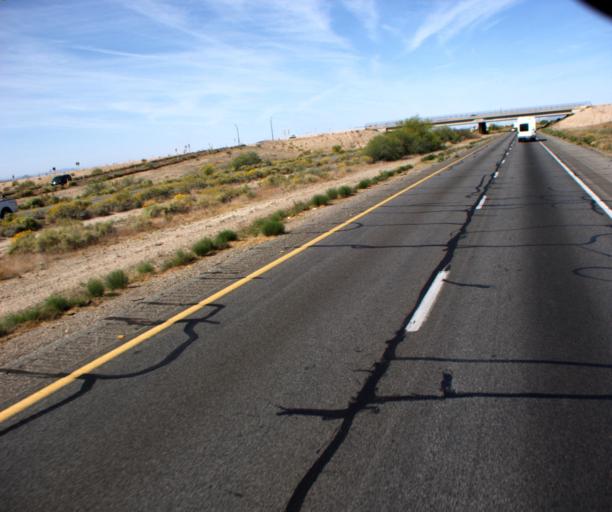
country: US
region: Arizona
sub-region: Maricopa County
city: Buckeye
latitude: 33.4387
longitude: -112.6742
